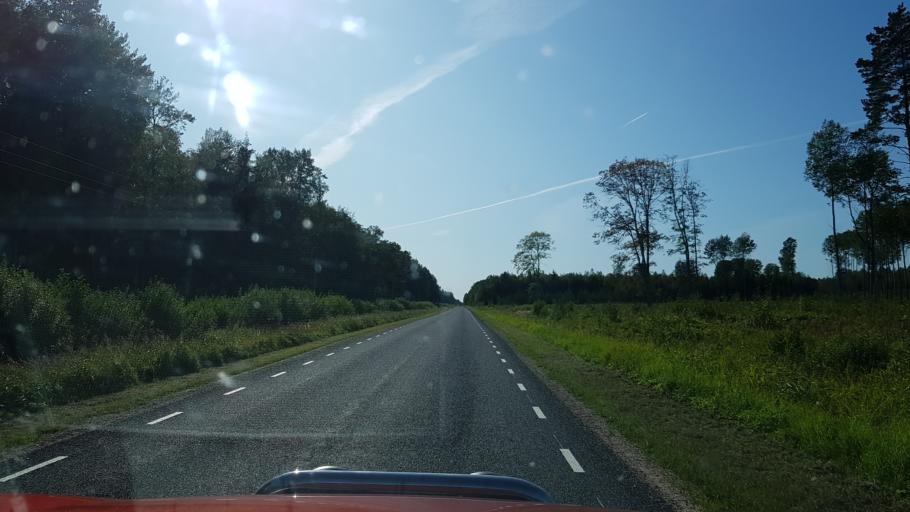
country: LV
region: Aloja
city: Staicele
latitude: 58.0870
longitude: 24.6142
